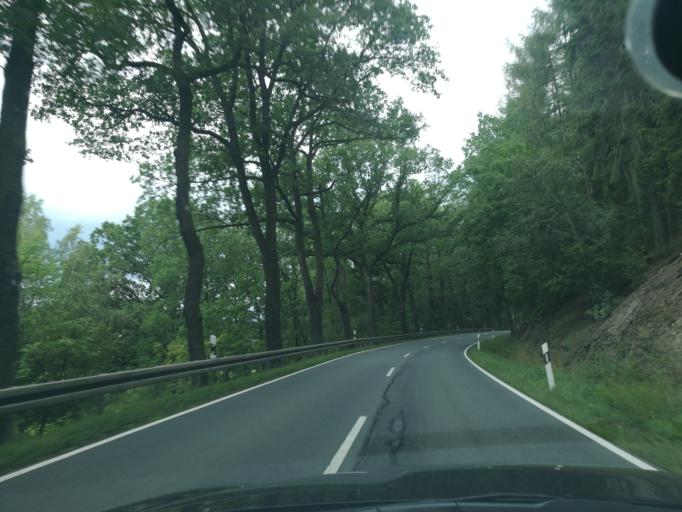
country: DE
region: Saxony
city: Eichigt
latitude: 50.3721
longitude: 12.2088
